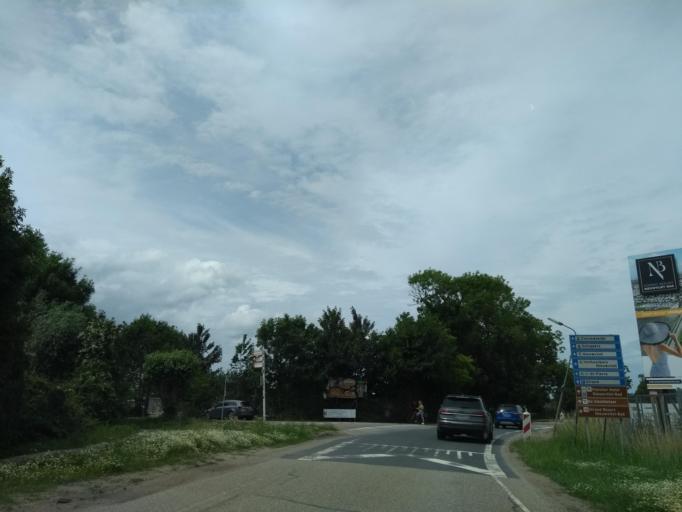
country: NL
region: Zeeland
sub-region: Gemeente Sluis
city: Sluis
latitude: 51.3801
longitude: 3.4584
